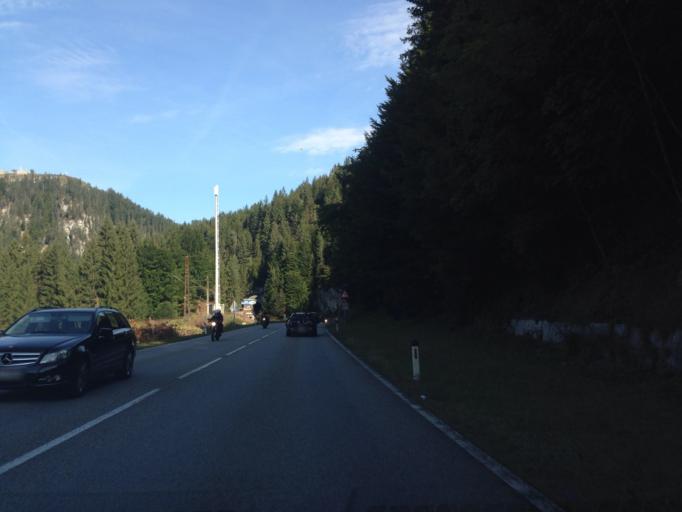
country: AT
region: Tyrol
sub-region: Politischer Bezirk Reutte
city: Ehenbichl
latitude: 47.4573
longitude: 10.7231
